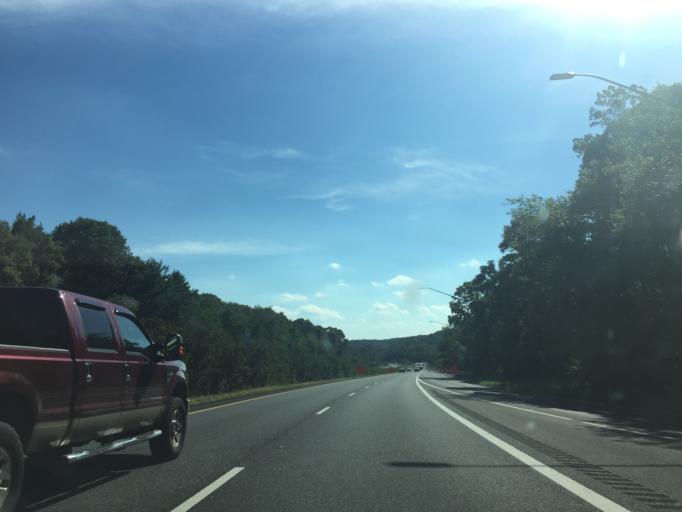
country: US
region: Pennsylvania
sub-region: York County
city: New Freedom
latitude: 39.6558
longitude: -76.6551
